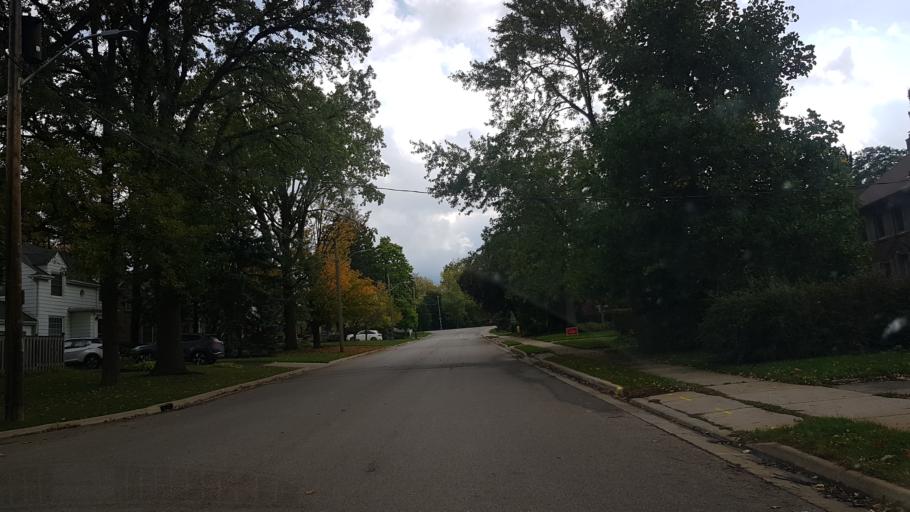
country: CA
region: Ontario
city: London
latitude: 42.9592
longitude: -81.2461
